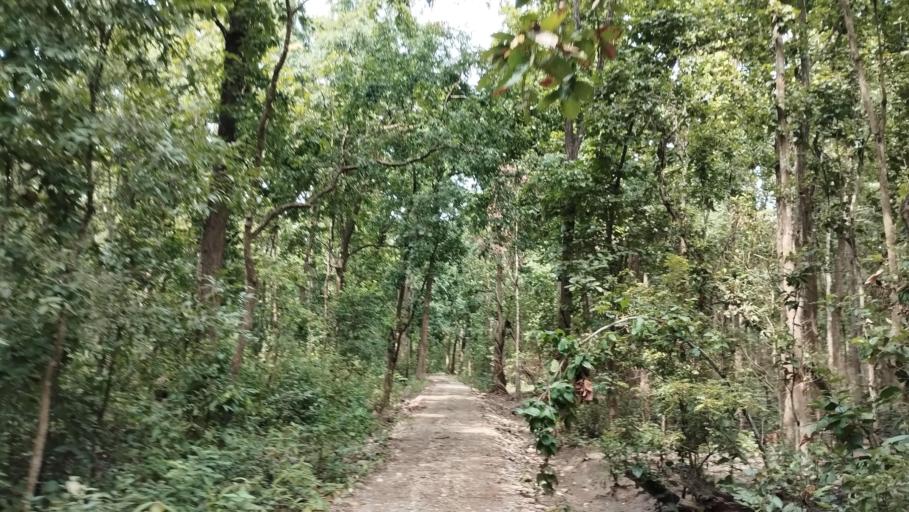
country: NP
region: Far Western
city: Tikapur
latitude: 28.4741
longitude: 81.2542
